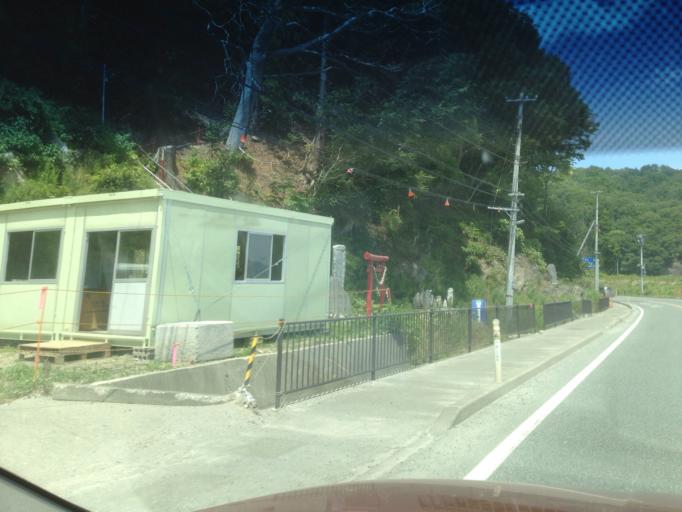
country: JP
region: Iwate
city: Otsuchi
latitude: 39.3375
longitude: 141.8920
